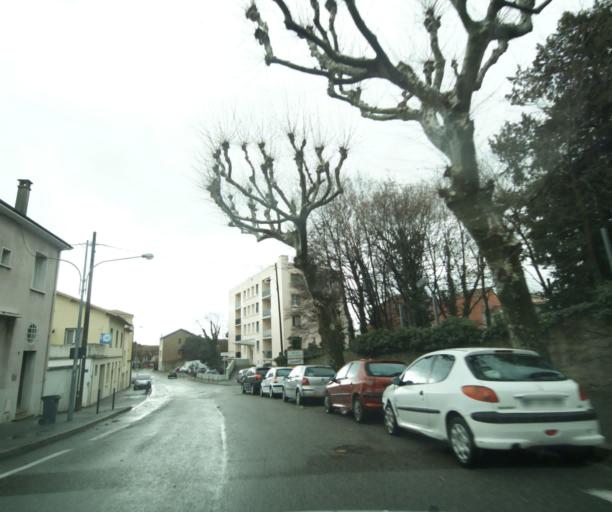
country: FR
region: Rhone-Alpes
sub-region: Departement de la Drome
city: Valence
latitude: 44.9369
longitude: 4.8934
